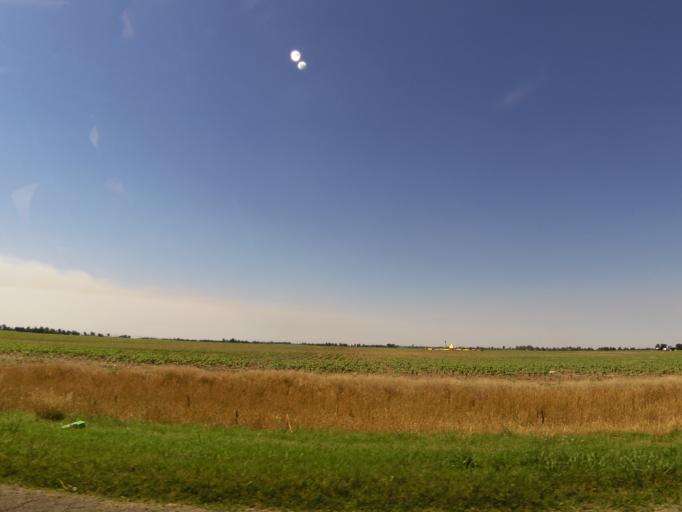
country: US
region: Missouri
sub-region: Dunklin County
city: Campbell
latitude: 36.4919
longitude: -90.0145
